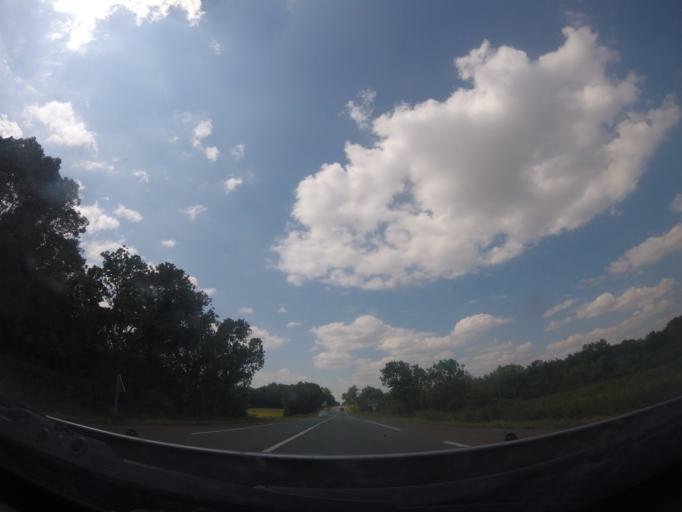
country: FR
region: Poitou-Charentes
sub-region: Departement de la Charente-Maritime
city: Saint-Porchaire
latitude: 45.8405
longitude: -0.8106
